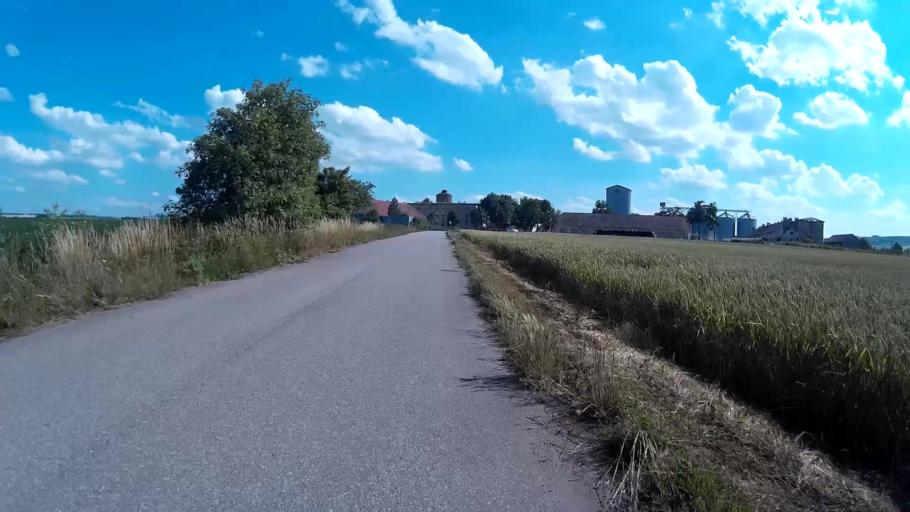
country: CZ
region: South Moravian
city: Menin
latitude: 49.0587
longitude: 16.7064
